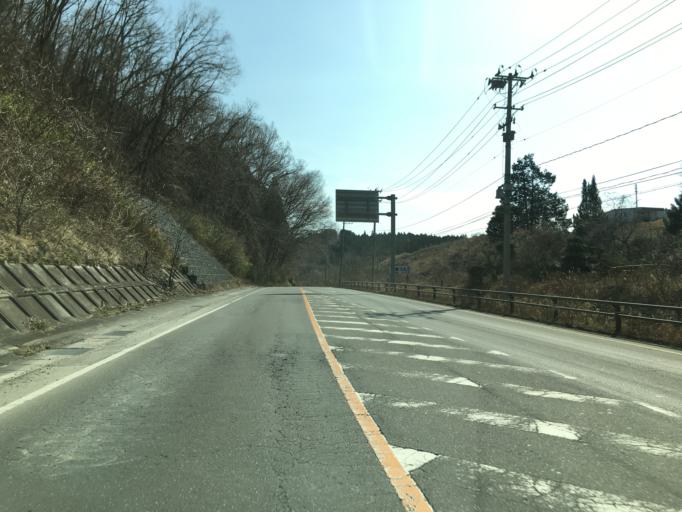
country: JP
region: Ibaraki
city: Daigo
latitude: 36.8530
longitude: 140.4307
